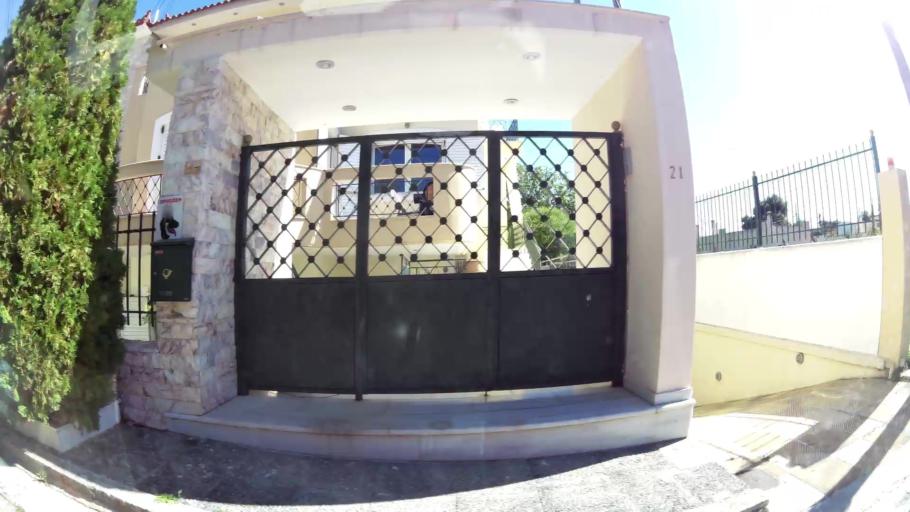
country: GR
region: Attica
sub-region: Nomarchia Anatolikis Attikis
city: Leondarion
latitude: 37.9934
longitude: 23.8585
